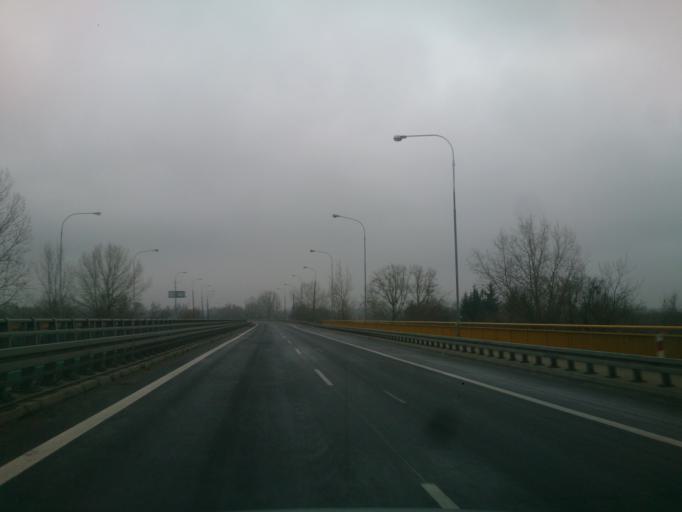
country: PL
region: Masovian Voivodeship
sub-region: Powiat nowodworski
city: Zakroczym
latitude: 52.4247
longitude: 20.6578
